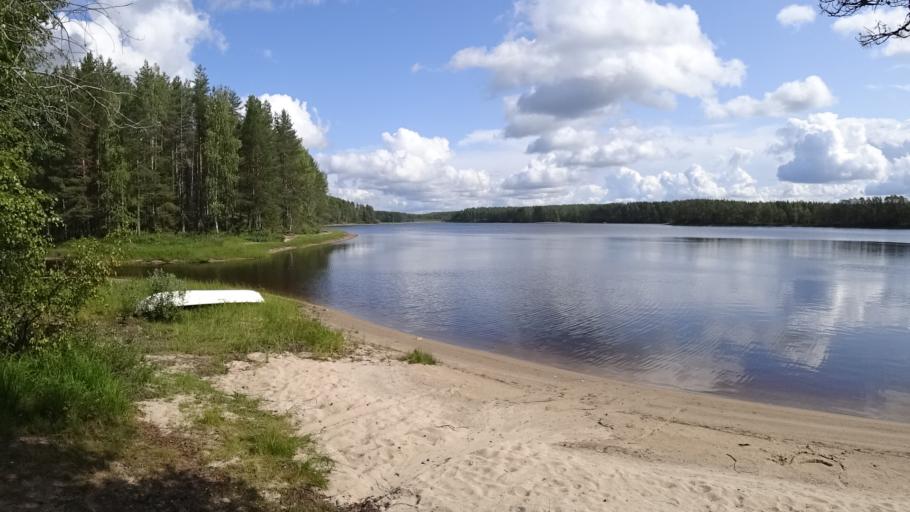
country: FI
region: North Karelia
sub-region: Joensuu
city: Ilomantsi
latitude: 62.6095
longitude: 31.1861
